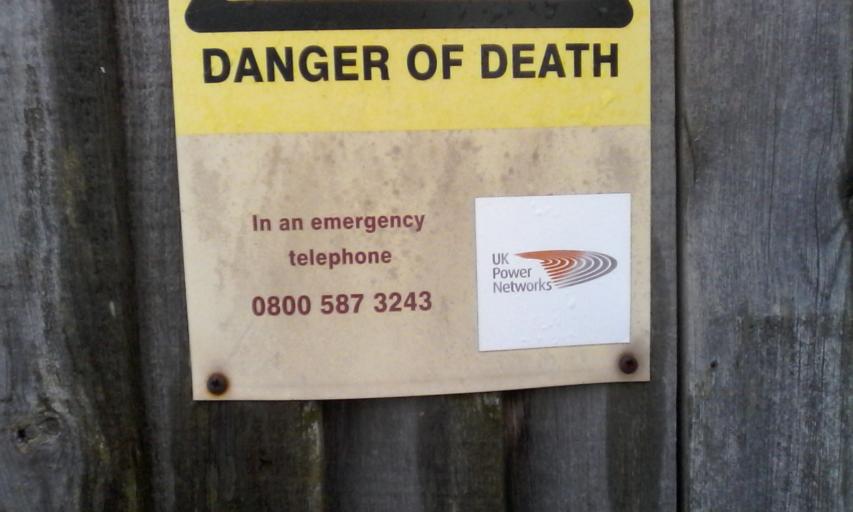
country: GB
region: England
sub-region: Hertfordshire
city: Ware
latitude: 51.8149
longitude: -0.0195
